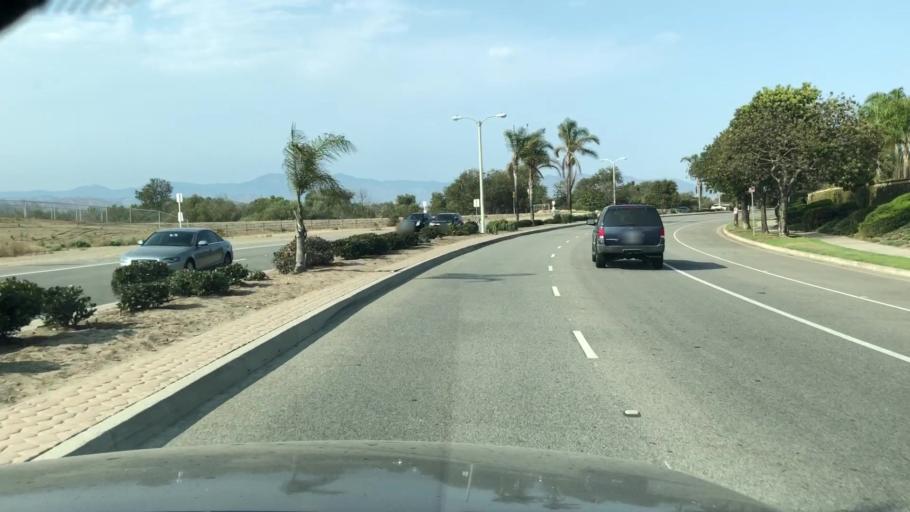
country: US
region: California
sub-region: Ventura County
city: El Rio
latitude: 34.2354
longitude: -119.1940
